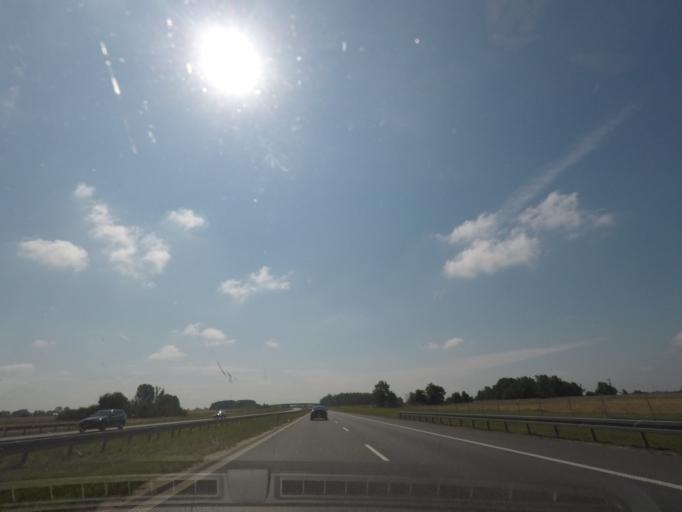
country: PL
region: Lodz Voivodeship
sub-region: Powiat kutnowski
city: Lanieta
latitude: 52.4186
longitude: 19.2615
